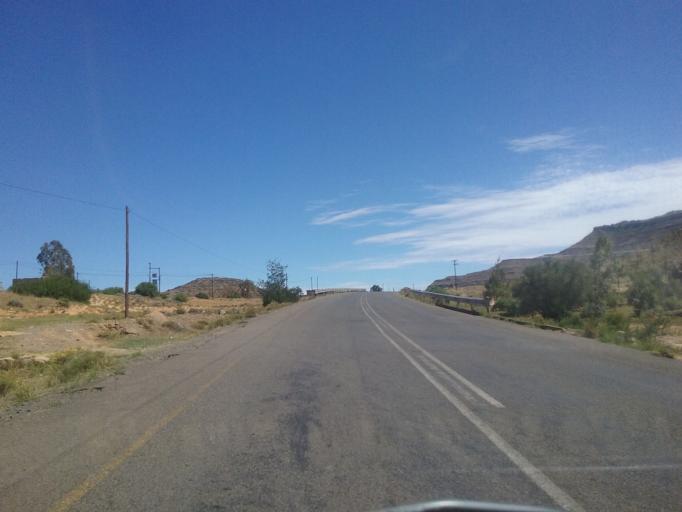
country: LS
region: Quthing
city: Quthing
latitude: -30.3567
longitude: 27.5461
